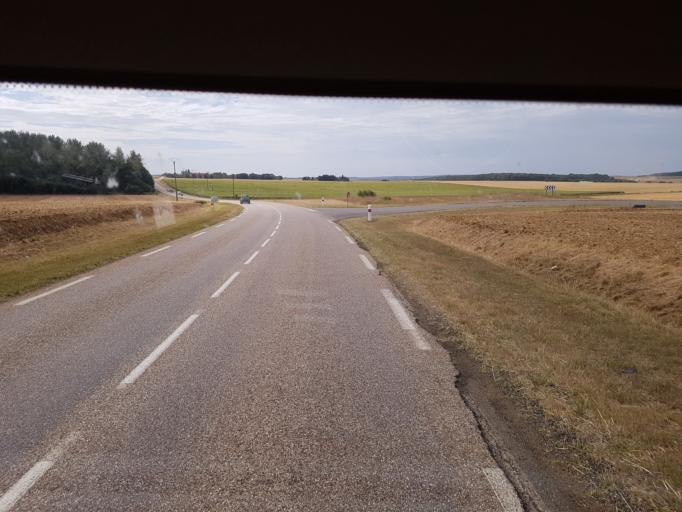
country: FR
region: Lorraine
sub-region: Departement de la Moselle
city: Amanvillers
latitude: 49.1387
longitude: 6.0115
